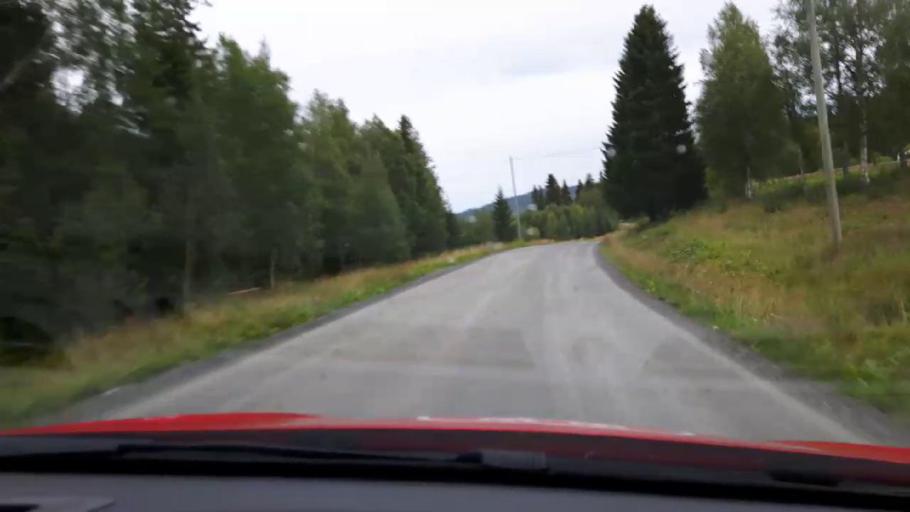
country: SE
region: Jaemtland
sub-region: Are Kommun
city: Jarpen
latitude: 63.4186
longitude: 13.3521
